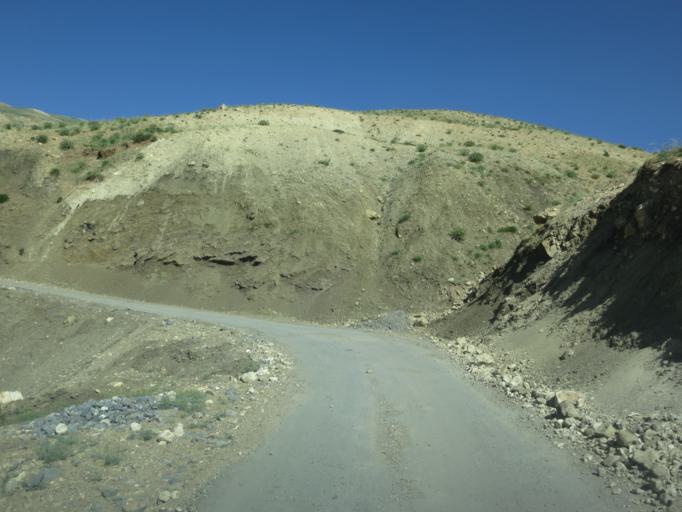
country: IN
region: Himachal Pradesh
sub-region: Kulu
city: Manali
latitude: 32.3248
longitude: 78.0070
